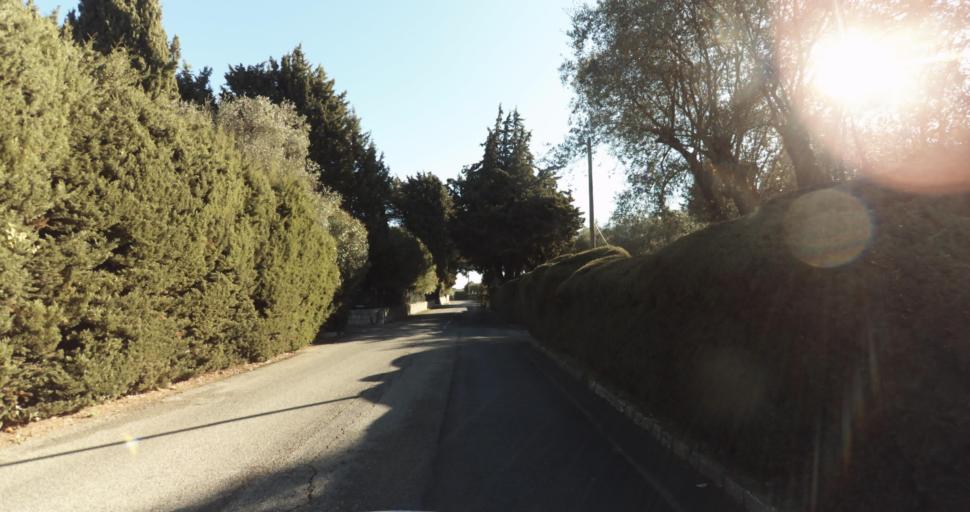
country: FR
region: Provence-Alpes-Cote d'Azur
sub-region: Departement des Alpes-Maritimes
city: Vence
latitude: 43.7246
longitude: 7.0841
